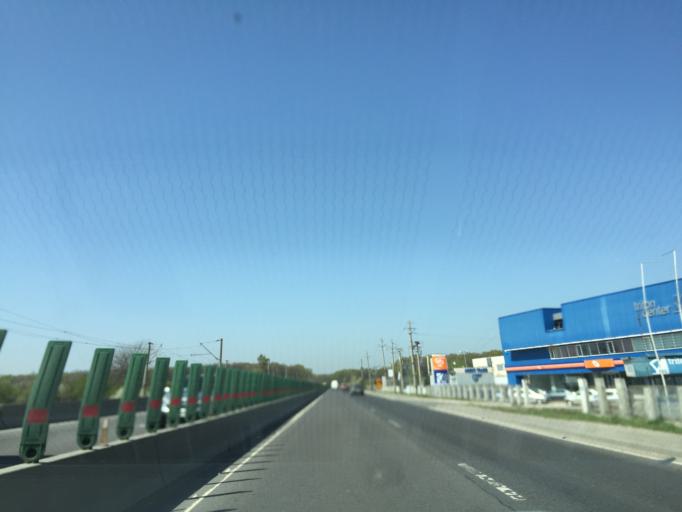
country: RO
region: Ilfov
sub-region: Comuna Tunari
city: Tunari
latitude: 44.5374
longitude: 26.1323
